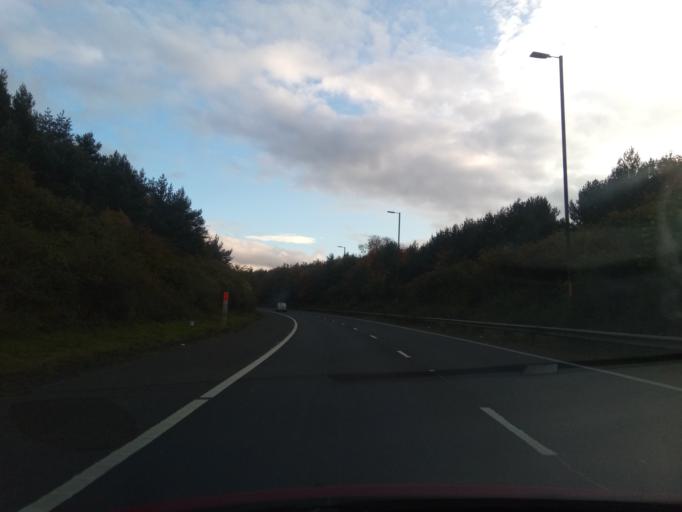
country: GB
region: Scotland
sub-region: Edinburgh
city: Newbridge
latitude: 55.9288
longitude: -3.4010
